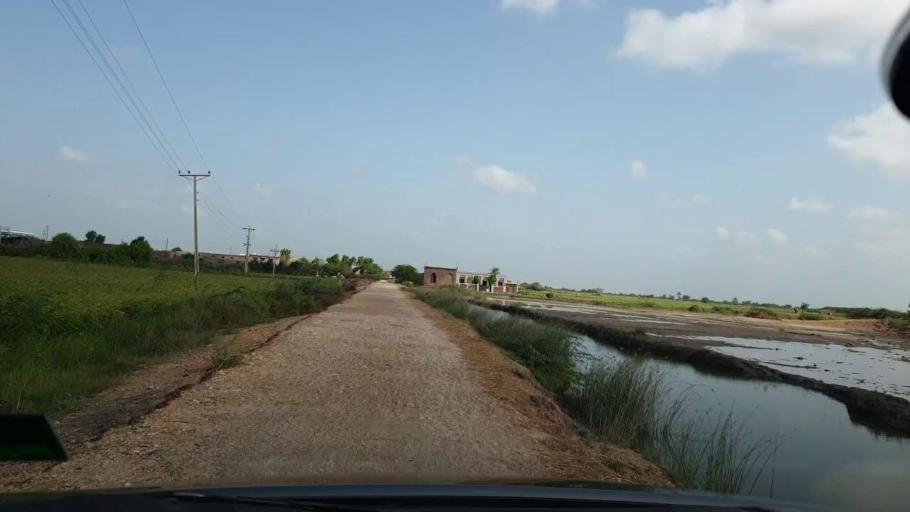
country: PK
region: Sindh
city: Tando Bago
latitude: 24.6427
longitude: 69.0937
